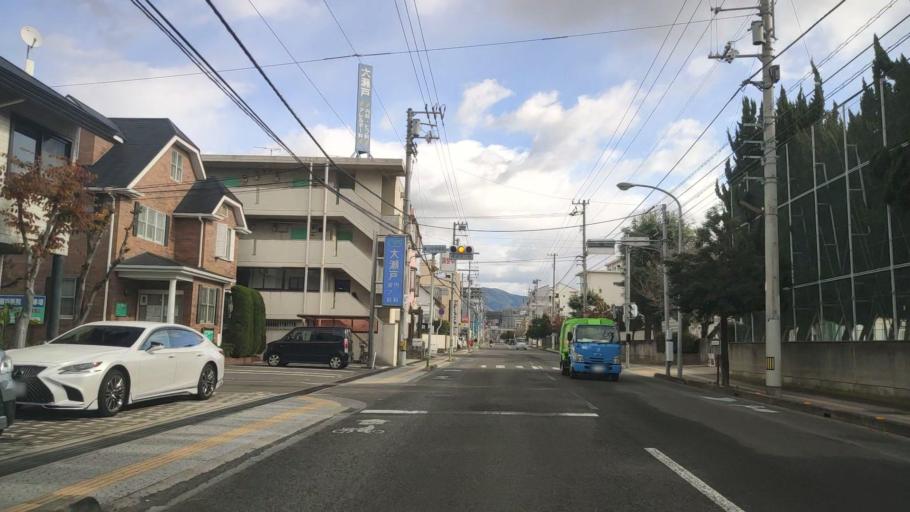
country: JP
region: Ehime
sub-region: Shikoku-chuo Shi
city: Matsuyama
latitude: 33.8525
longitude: 132.7636
